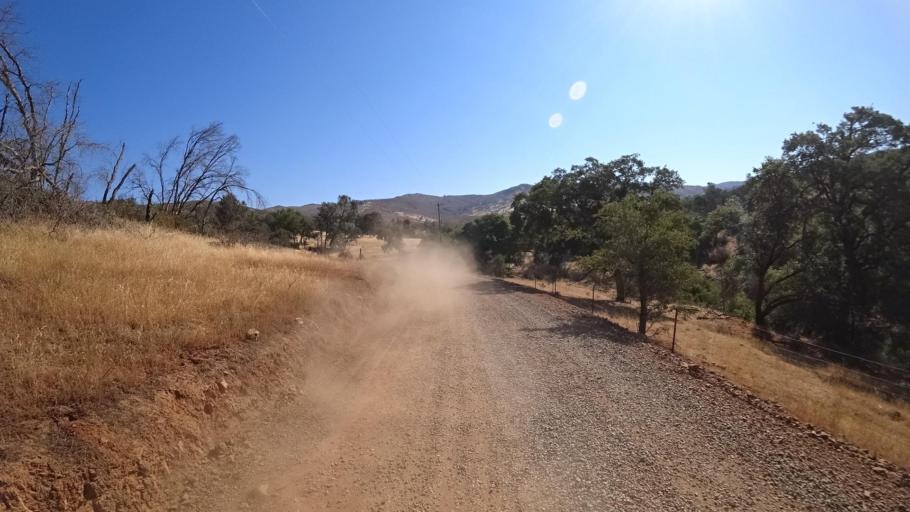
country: US
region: California
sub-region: Mariposa County
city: Mariposa
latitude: 37.6171
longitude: -120.2295
